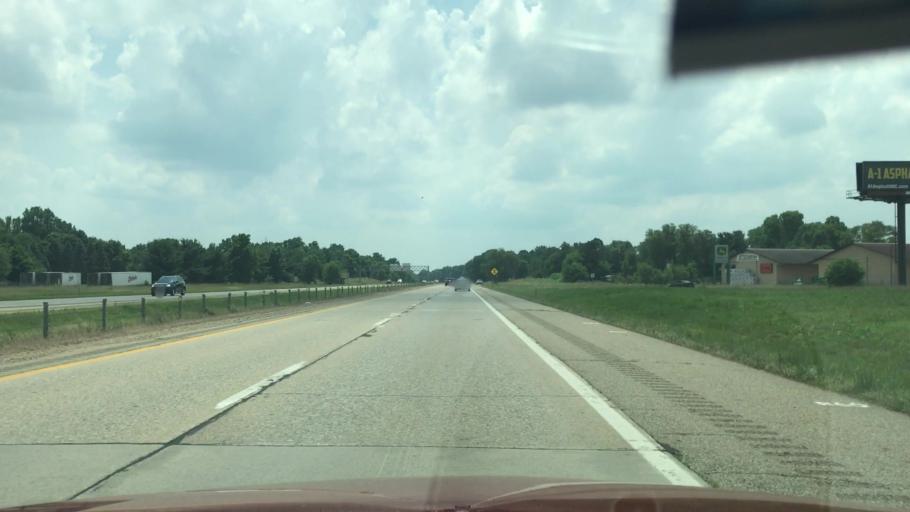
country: US
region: Michigan
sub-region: Allegan County
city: Plainwell
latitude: 42.4481
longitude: -85.6571
